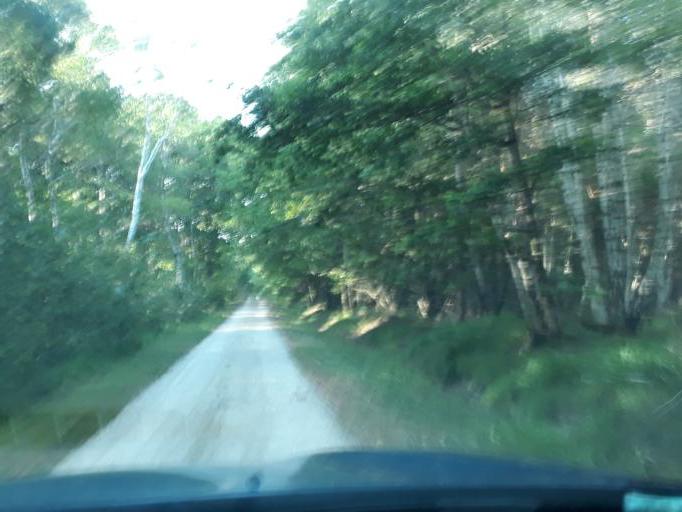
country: FR
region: Centre
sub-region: Departement du Loiret
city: Chaingy
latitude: 47.9127
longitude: 1.7417
